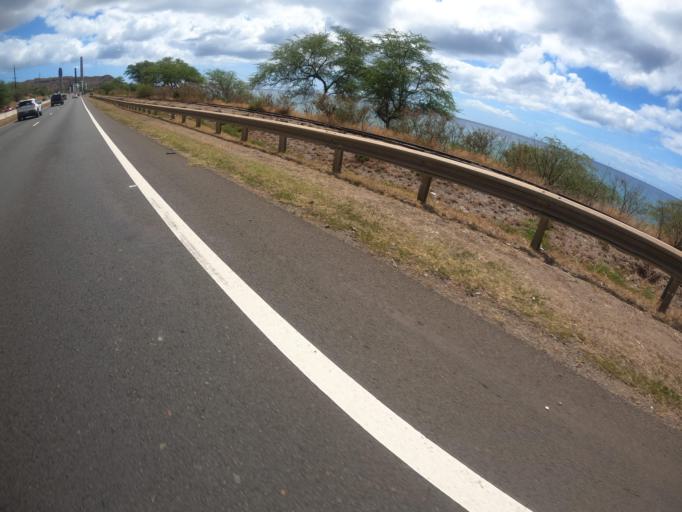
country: US
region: Hawaii
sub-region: Honolulu County
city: Nanakuli
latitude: 21.3655
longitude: -158.1345
